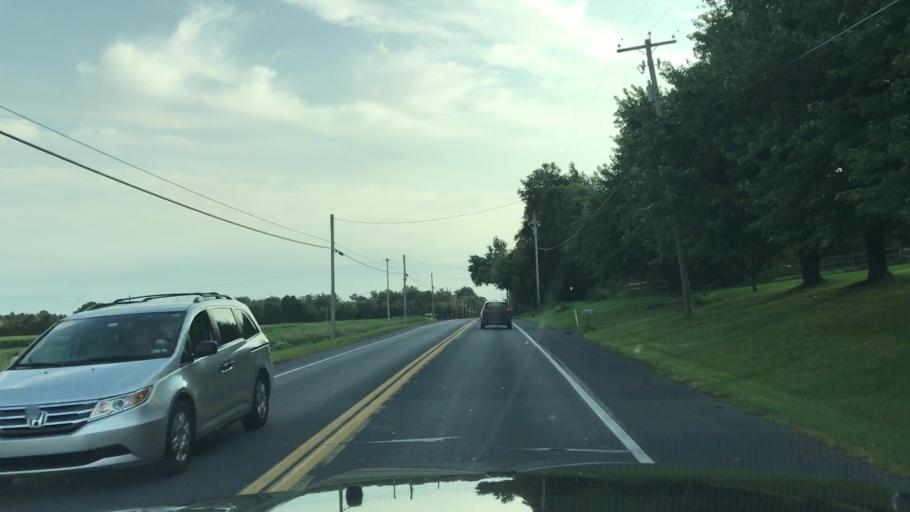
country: US
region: Pennsylvania
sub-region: Berks County
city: Bally
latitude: 40.4123
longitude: -75.5783
